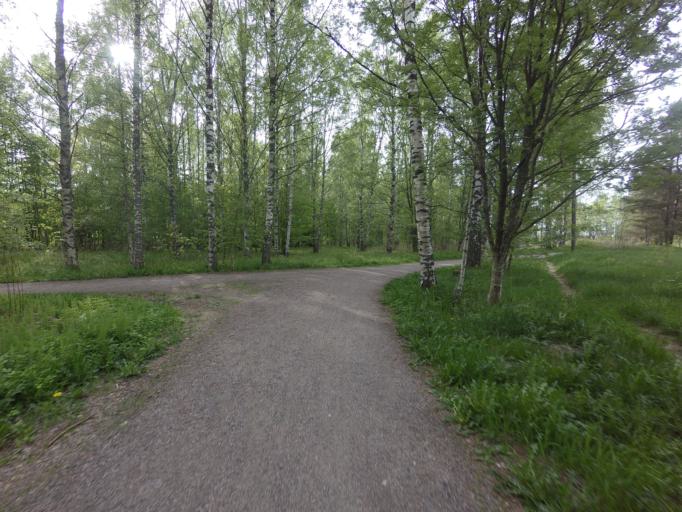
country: FI
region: Uusimaa
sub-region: Helsinki
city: Koukkuniemi
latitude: 60.1512
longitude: 24.6990
